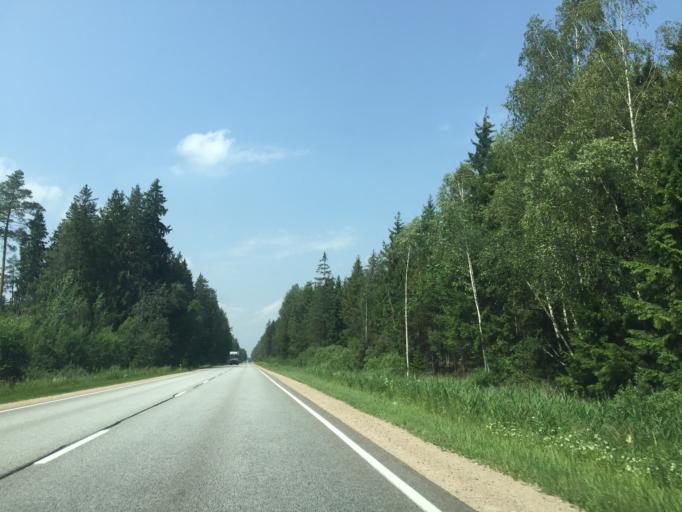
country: LV
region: Kekava
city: Balozi
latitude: 56.8135
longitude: 24.1481
